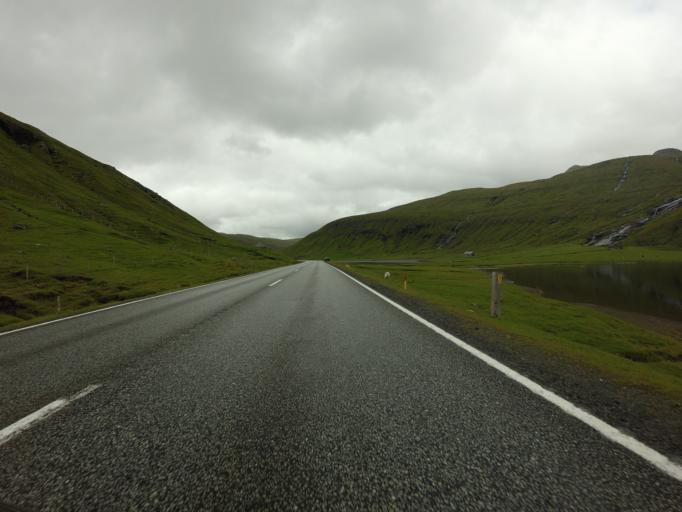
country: FO
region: Streymoy
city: Kollafjordhur
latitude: 62.1247
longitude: -6.9966
